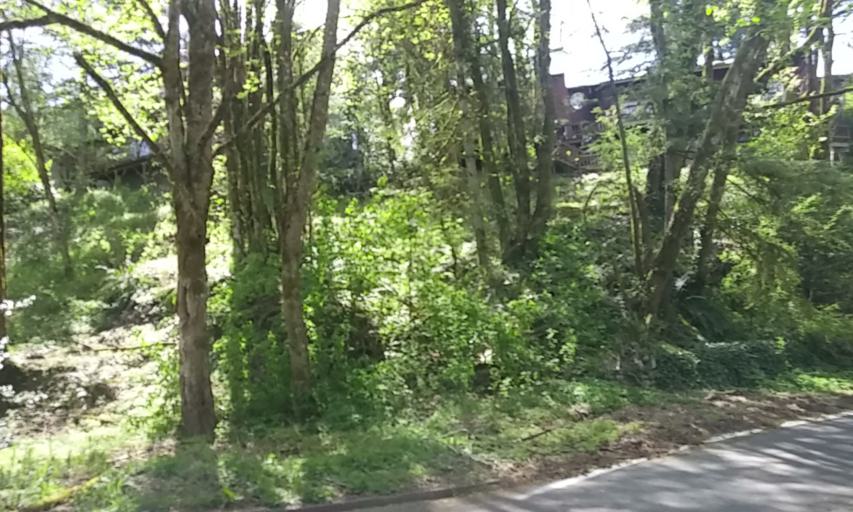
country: US
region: Oregon
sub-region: Washington County
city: West Haven-Sylvan
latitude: 45.5150
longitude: -122.7399
